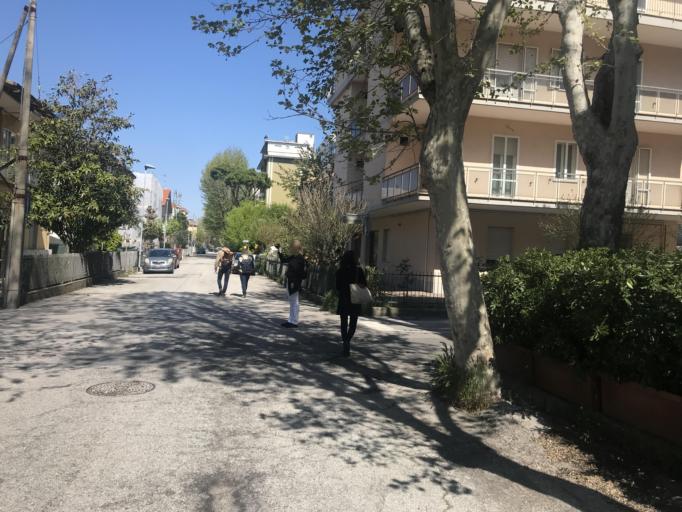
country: IT
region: Emilia-Romagna
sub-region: Provincia di Rimini
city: Rimini
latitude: 44.0756
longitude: 12.5538
